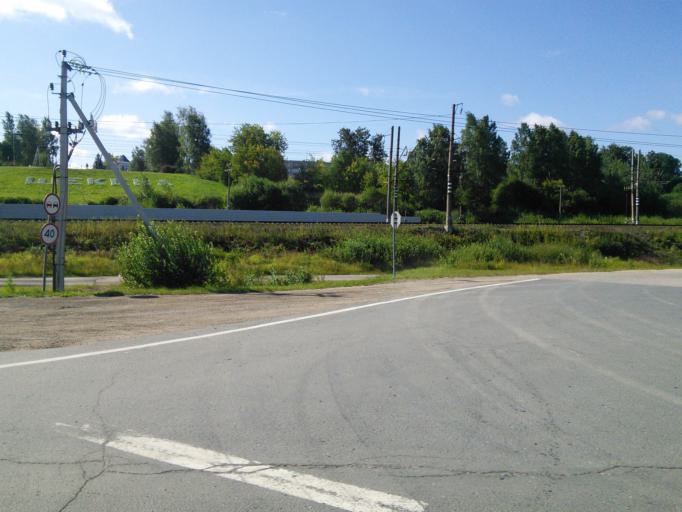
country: RU
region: Vologda
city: Sheksna
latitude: 59.2100
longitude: 38.5009
